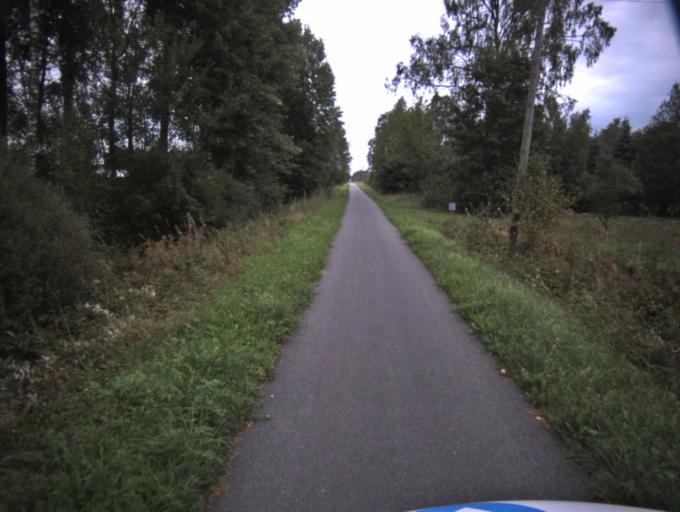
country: SE
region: Vaestra Goetaland
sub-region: Ulricehamns Kommun
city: Ulricehamn
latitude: 57.9534
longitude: 13.5080
